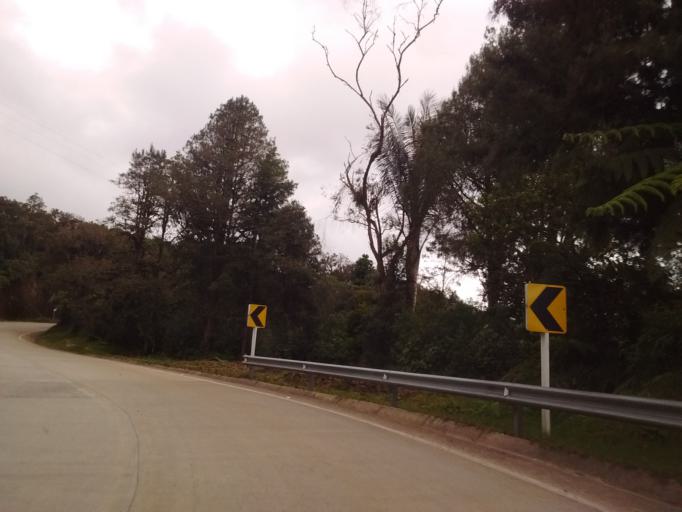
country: CO
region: Huila
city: Isnos
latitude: 2.0451
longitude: -76.2872
